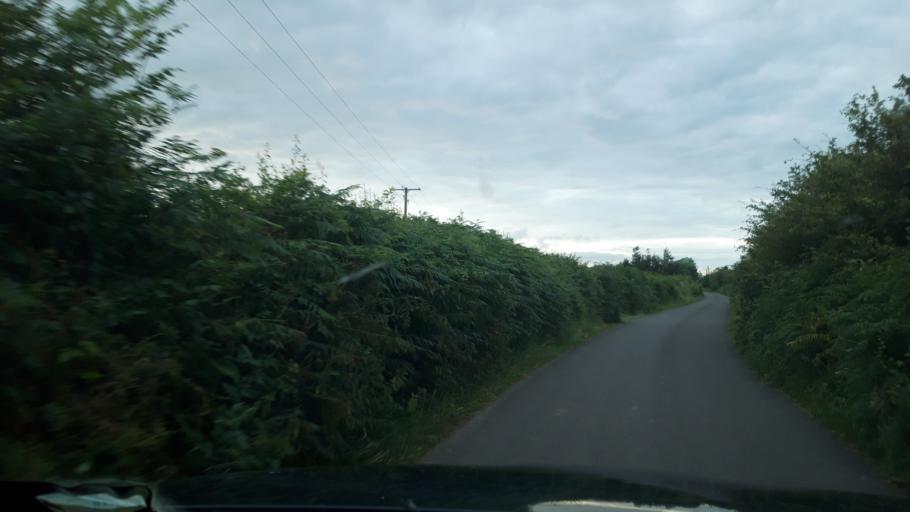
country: IE
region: Leinster
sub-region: Kilkenny
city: Graiguenamanagh
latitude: 52.5854
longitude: -6.9951
